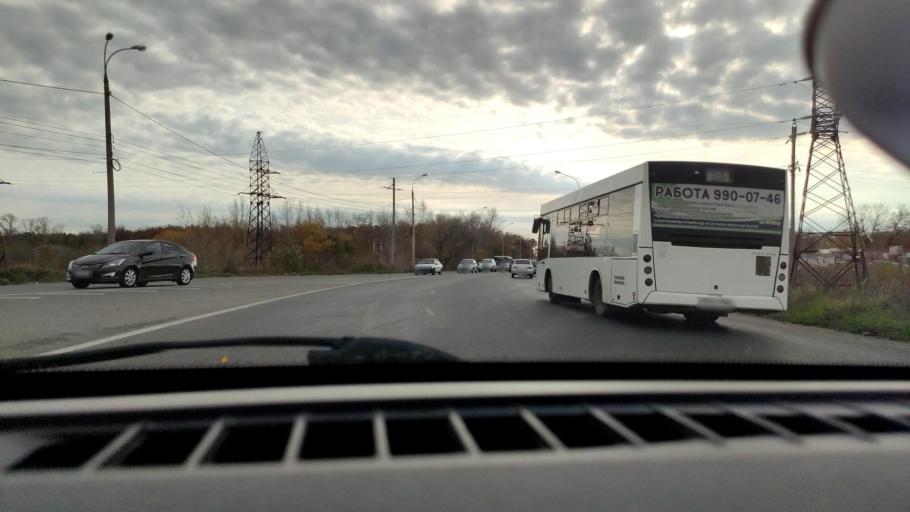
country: RU
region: Samara
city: Samara
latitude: 53.1336
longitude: 50.1736
